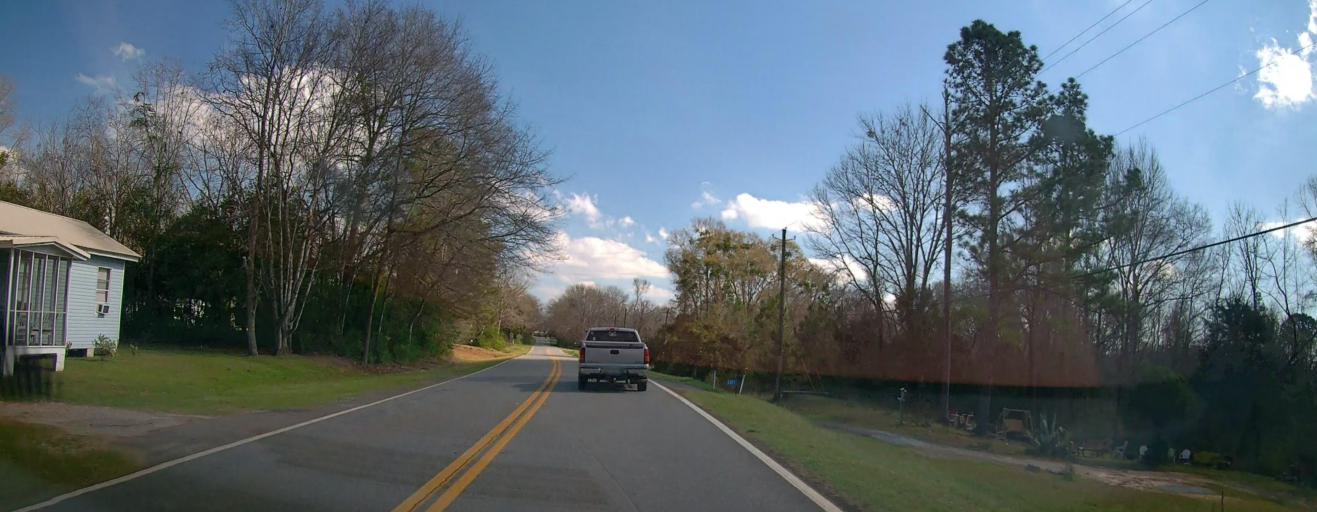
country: US
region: Georgia
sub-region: Twiggs County
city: Jeffersonville
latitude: 32.6955
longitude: -83.3469
